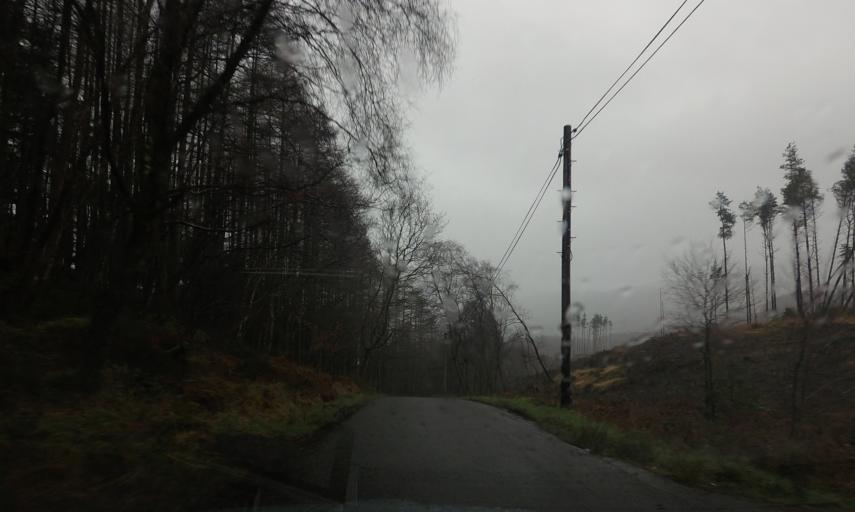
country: GB
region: Scotland
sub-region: West Dunbartonshire
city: Balloch
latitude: 56.1459
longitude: -4.6387
